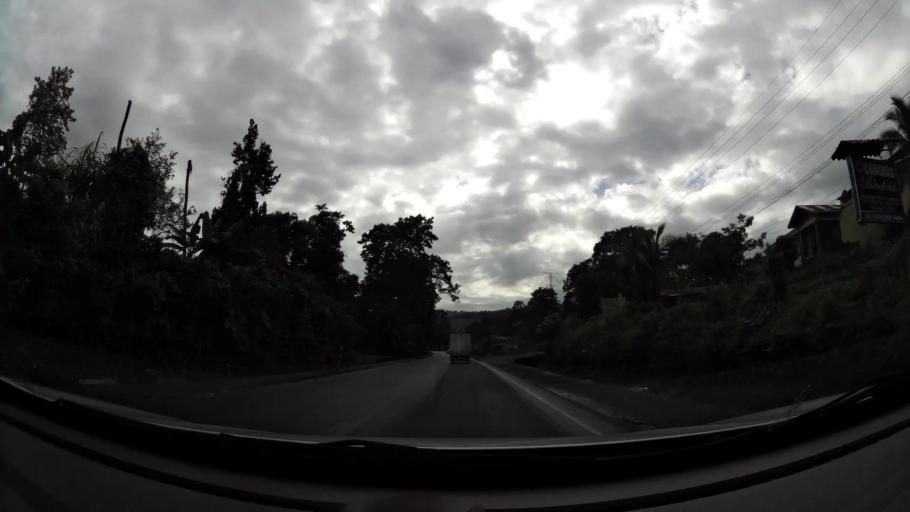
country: CR
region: Limon
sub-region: Canton de Siquirres
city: Siquirres
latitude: 10.0944
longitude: -83.5098
